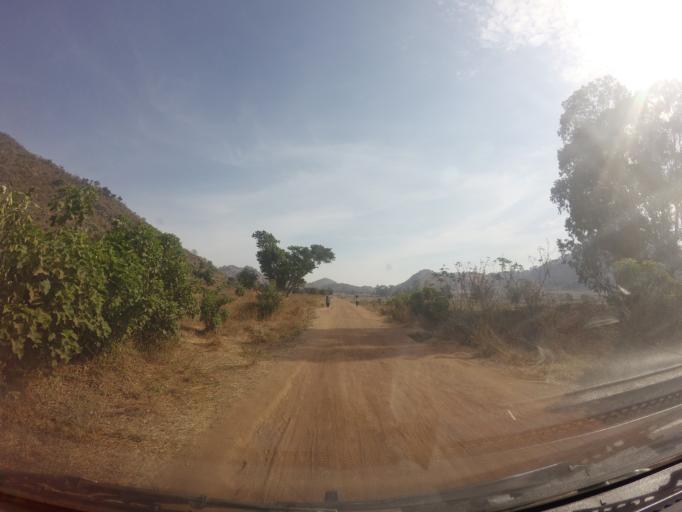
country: UG
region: Northern Region
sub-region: Maracha District
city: Maracha
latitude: 3.2093
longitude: 31.0372
